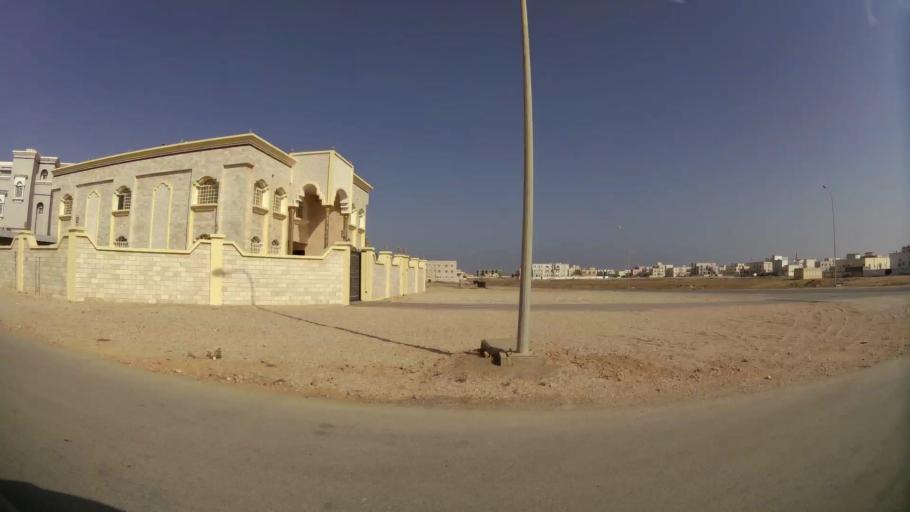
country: OM
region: Zufar
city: Salalah
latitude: 17.0084
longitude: 54.0149
